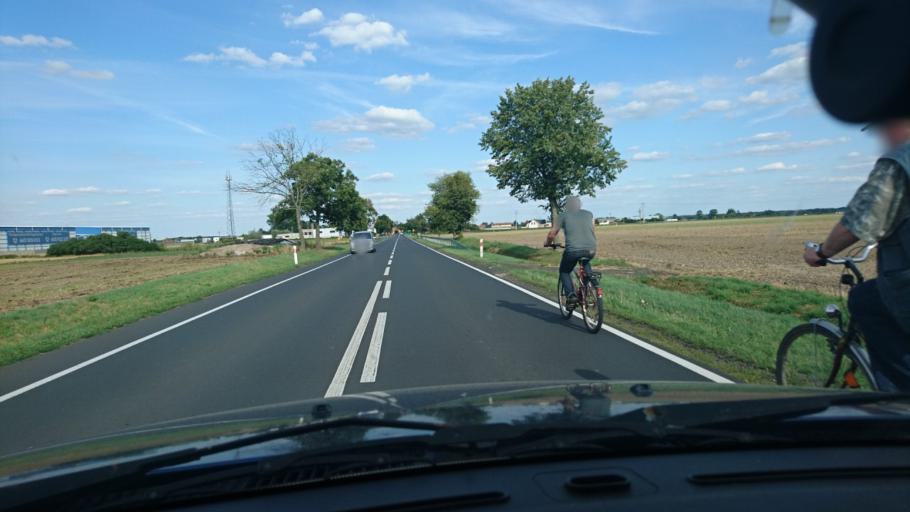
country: PL
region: Greater Poland Voivodeship
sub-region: Powiat krotoszynski
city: Kobylin
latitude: 51.7101
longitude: 17.2051
